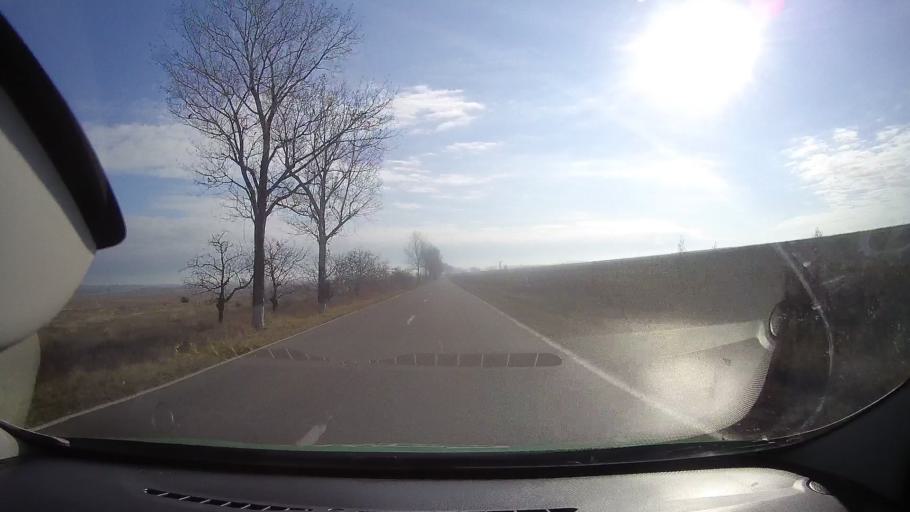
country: RO
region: Tulcea
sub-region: Comuna Mahmudia
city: Mahmudia
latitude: 45.0711
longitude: 29.0961
